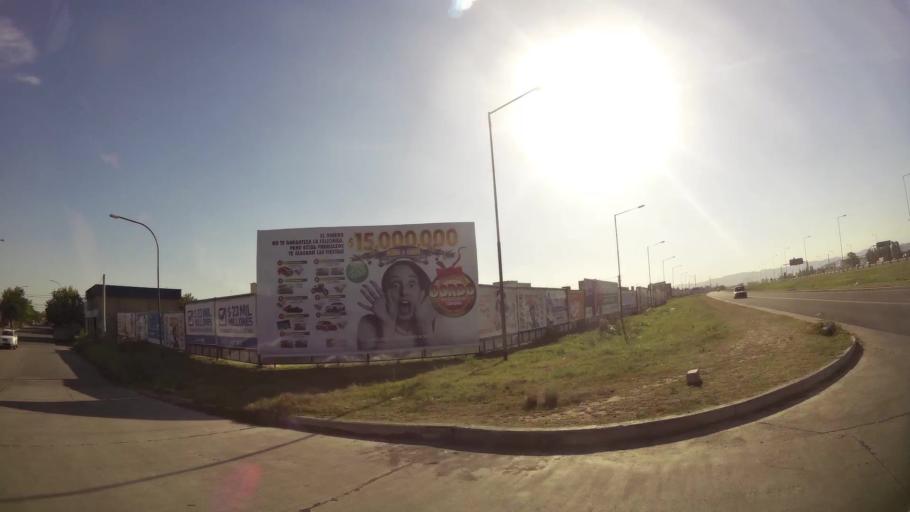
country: AR
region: Cordoba
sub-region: Departamento de Capital
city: Cordoba
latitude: -31.3556
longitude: -64.2127
